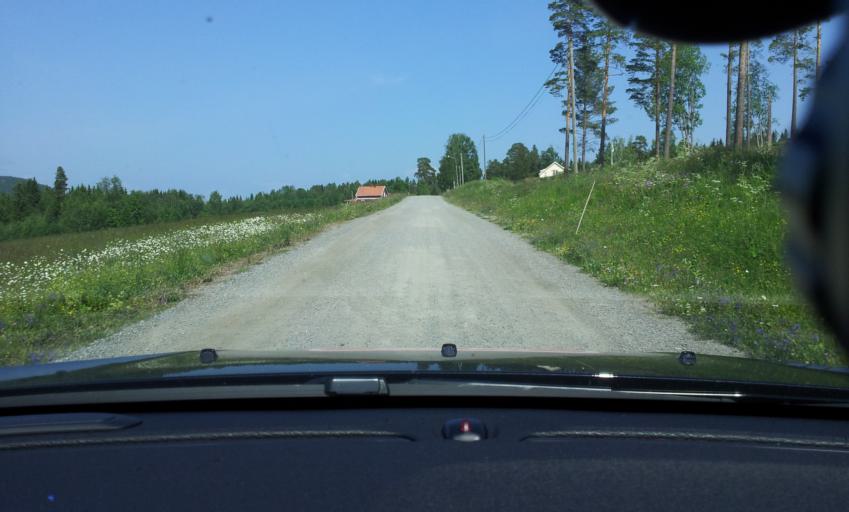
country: SE
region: Jaemtland
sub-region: Bergs Kommun
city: Hoverberg
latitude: 62.7931
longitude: 14.4613
